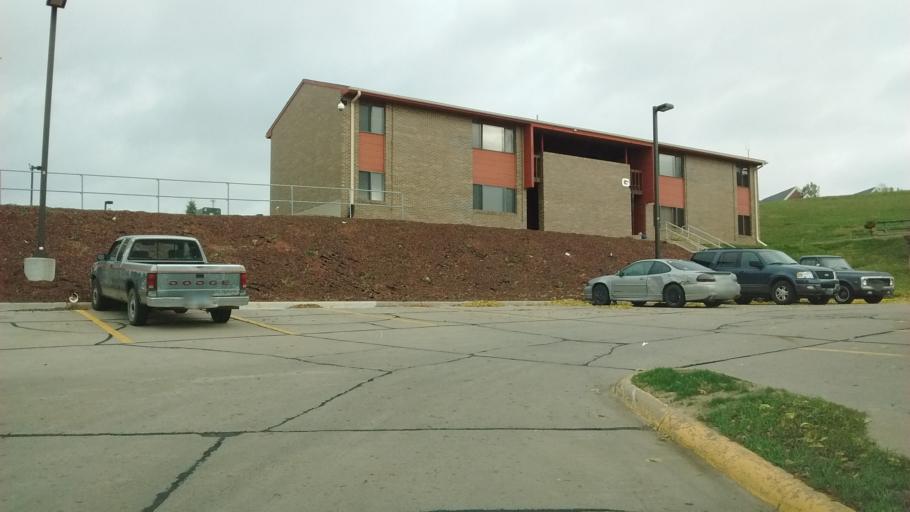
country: US
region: Iowa
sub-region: Woodbury County
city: Sioux City
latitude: 42.4800
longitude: -96.3451
